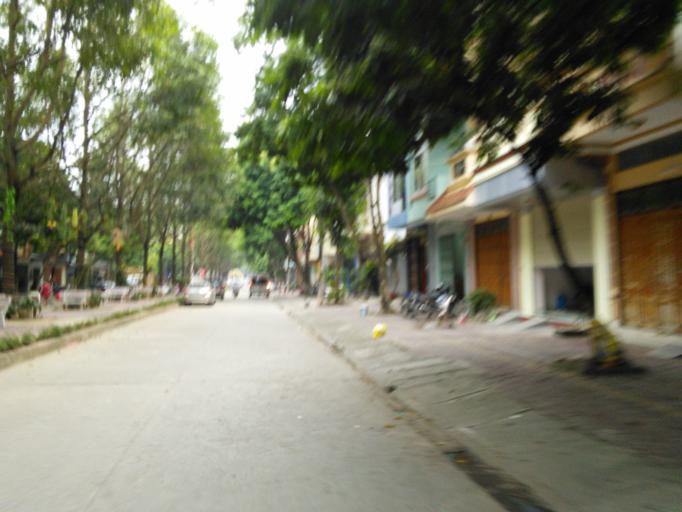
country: VN
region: Lao Cai
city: Lao Cai
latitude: 22.4960
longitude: 103.9744
